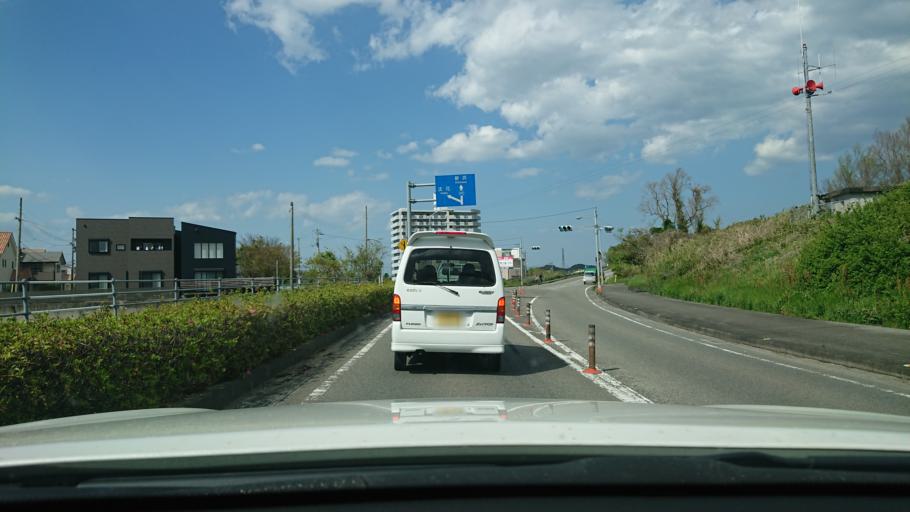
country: JP
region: Tokushima
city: Komatsushimacho
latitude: 34.0133
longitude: 134.5556
